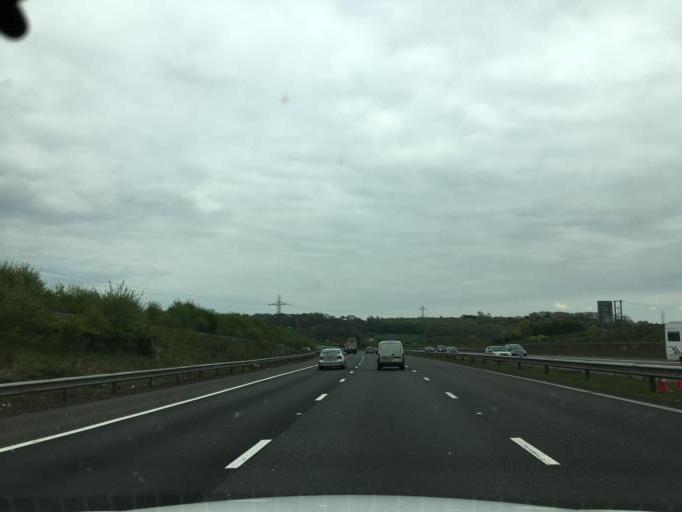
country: GB
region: Wales
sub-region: Newport
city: Marshfield
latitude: 51.5414
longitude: -3.1257
